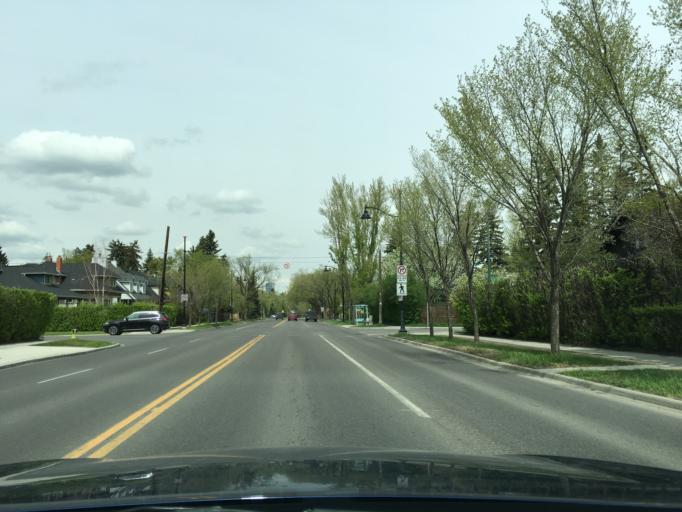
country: CA
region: Alberta
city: Calgary
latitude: 51.0212
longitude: -114.0778
